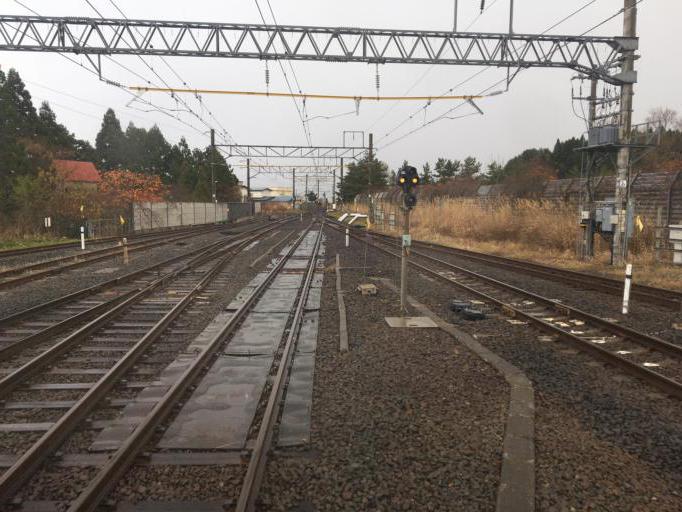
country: JP
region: Aomori
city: Aomori Shi
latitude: 41.0377
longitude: 140.6433
